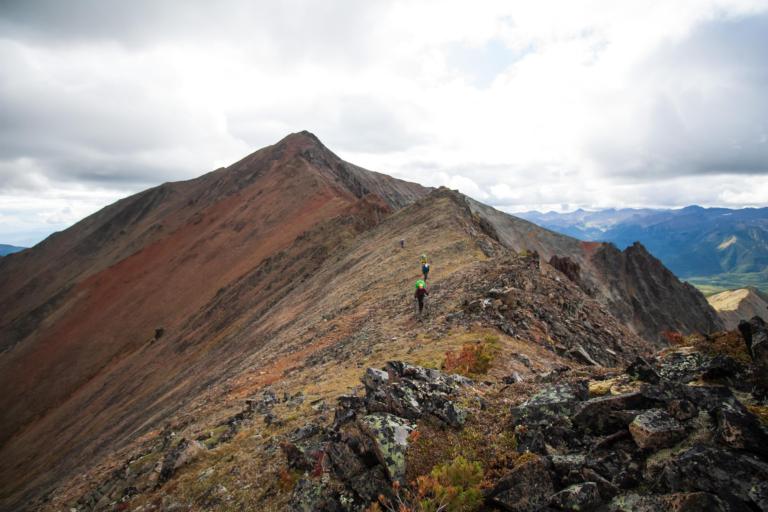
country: RU
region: Kamtsjatka
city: Yelizovo
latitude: 53.8432
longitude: 158.1870
